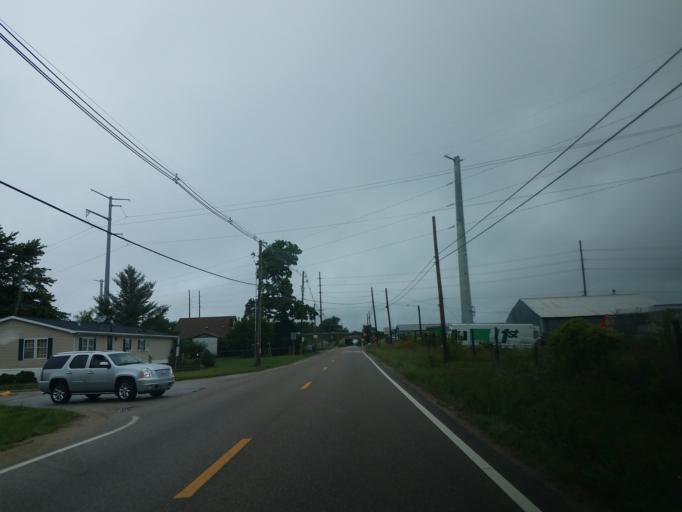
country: US
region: Illinois
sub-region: McLean County
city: Bloomington
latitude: 40.4566
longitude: -88.9814
